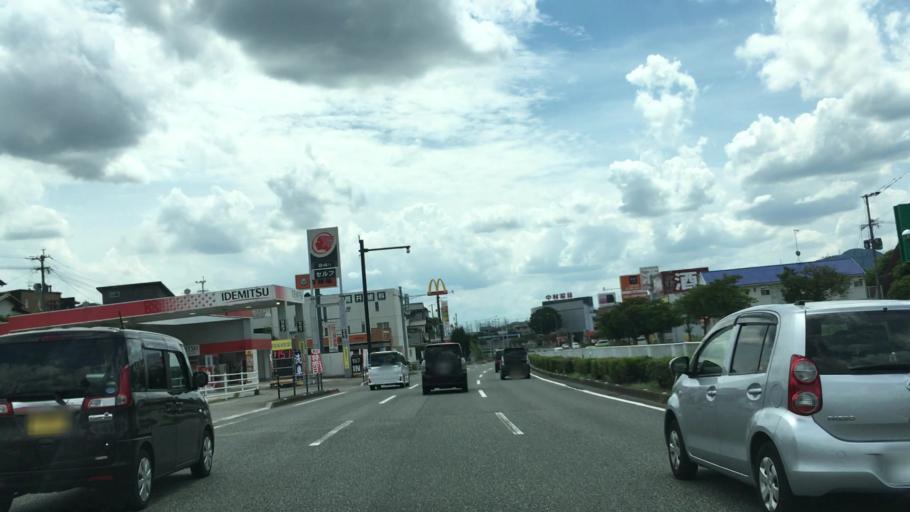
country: JP
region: Fukuoka
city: Dazaifu
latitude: 33.5027
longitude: 130.5313
